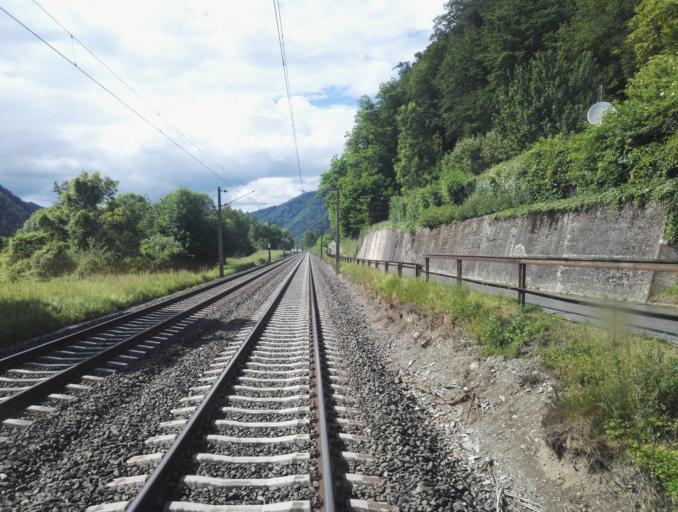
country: AT
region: Styria
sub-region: Politischer Bezirk Bruck-Muerzzuschlag
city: Pernegg an der Mur
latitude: 47.3451
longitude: 15.3526
